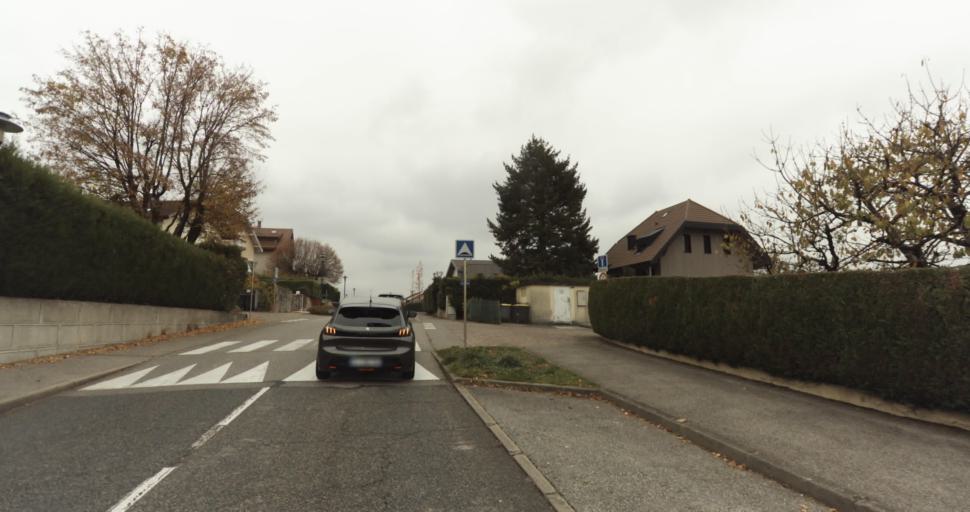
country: FR
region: Rhone-Alpes
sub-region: Departement de la Haute-Savoie
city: Annecy-le-Vieux
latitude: 45.9227
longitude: 6.1373
